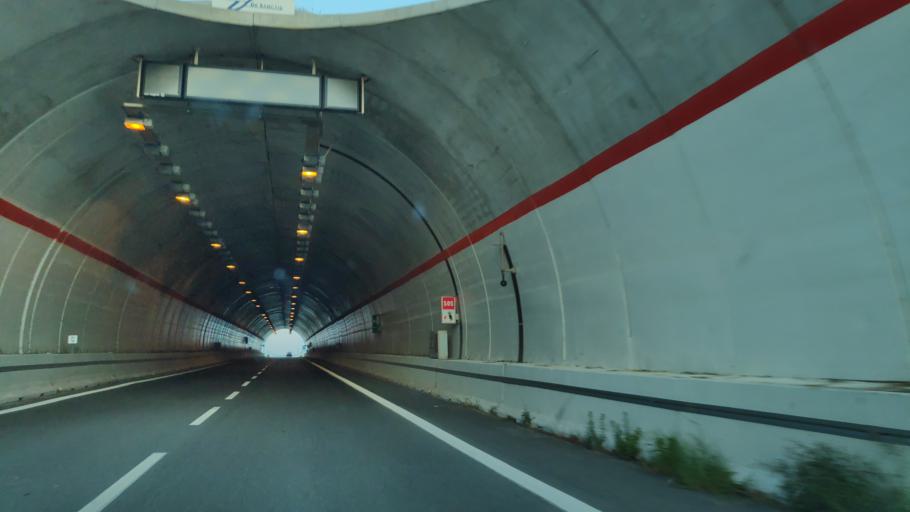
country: IT
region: Calabria
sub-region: Provincia di Reggio Calabria
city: Marina di Gioiosa Ionica
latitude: 38.3117
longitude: 16.3434
